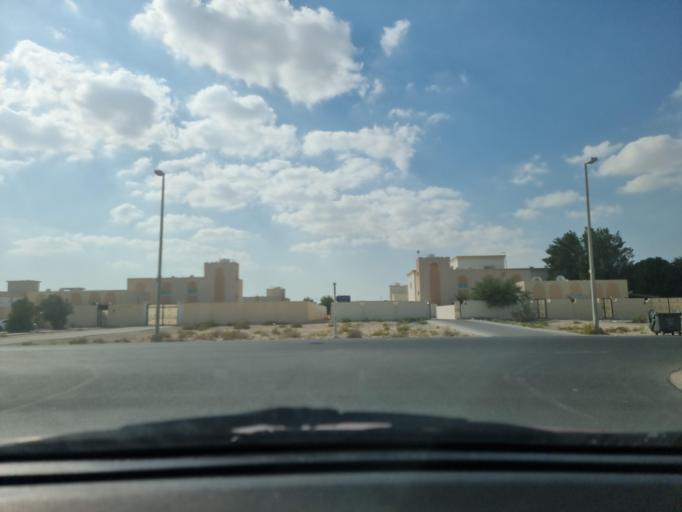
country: AE
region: Abu Dhabi
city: Abu Dhabi
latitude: 24.3832
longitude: 54.7019
